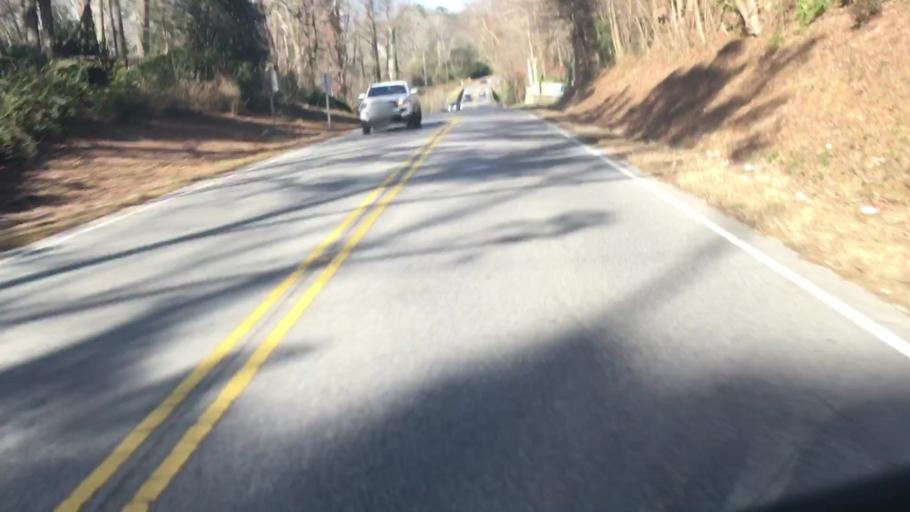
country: US
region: Alabama
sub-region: Shelby County
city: Meadowbrook
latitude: 33.4134
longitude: -86.7406
